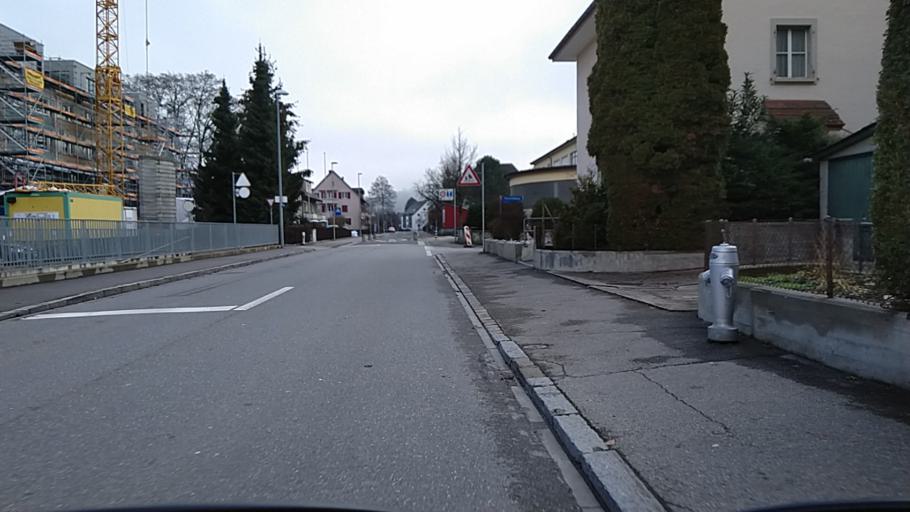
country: CH
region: Bern
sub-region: Bern-Mittelland District
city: Wohlen
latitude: 46.9451
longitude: 7.3832
